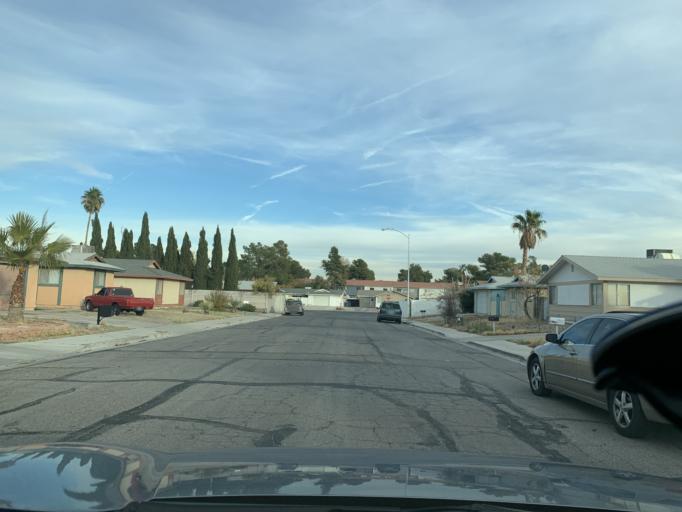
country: US
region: Nevada
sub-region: Clark County
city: Spring Valley
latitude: 36.0986
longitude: -115.2319
